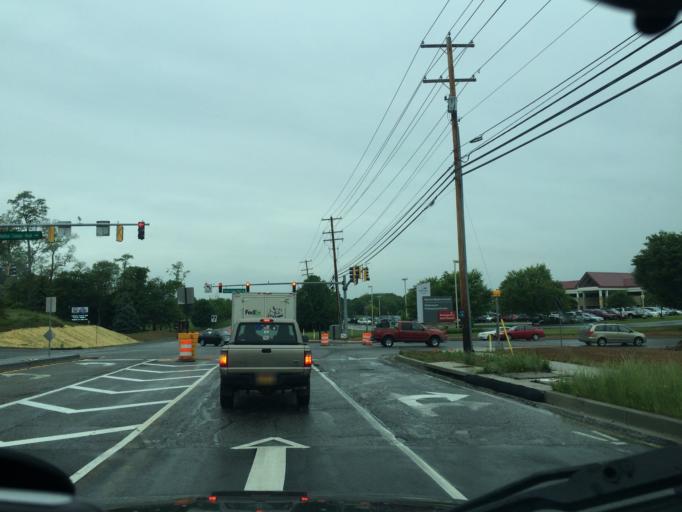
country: US
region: Maryland
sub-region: Washington County
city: Robinwood
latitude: 39.6211
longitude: -77.6790
